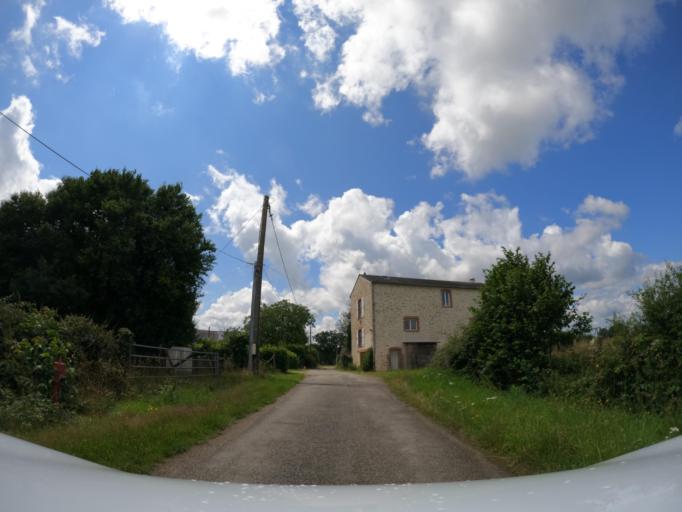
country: FR
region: Pays de la Loire
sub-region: Departement de la Loire-Atlantique
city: Saint-Mars-du-Desert
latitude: 47.3872
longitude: -1.4175
